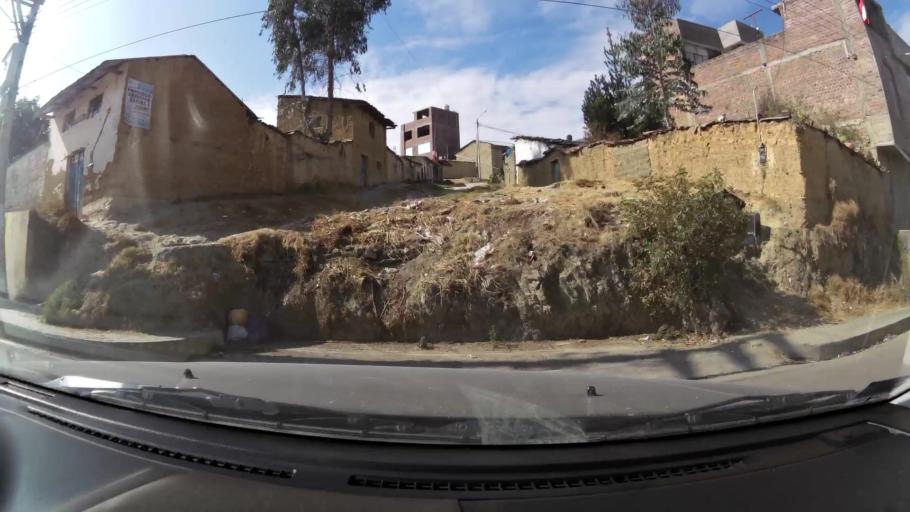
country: PE
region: Junin
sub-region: Provincia de Huancayo
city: Huancayo
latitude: -12.0586
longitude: -75.1964
